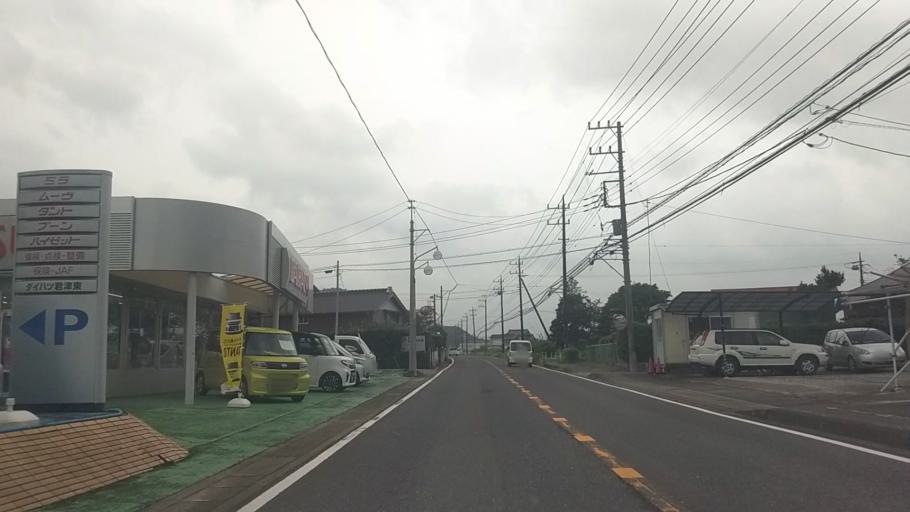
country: JP
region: Chiba
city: Kisarazu
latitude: 35.3098
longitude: 140.0655
